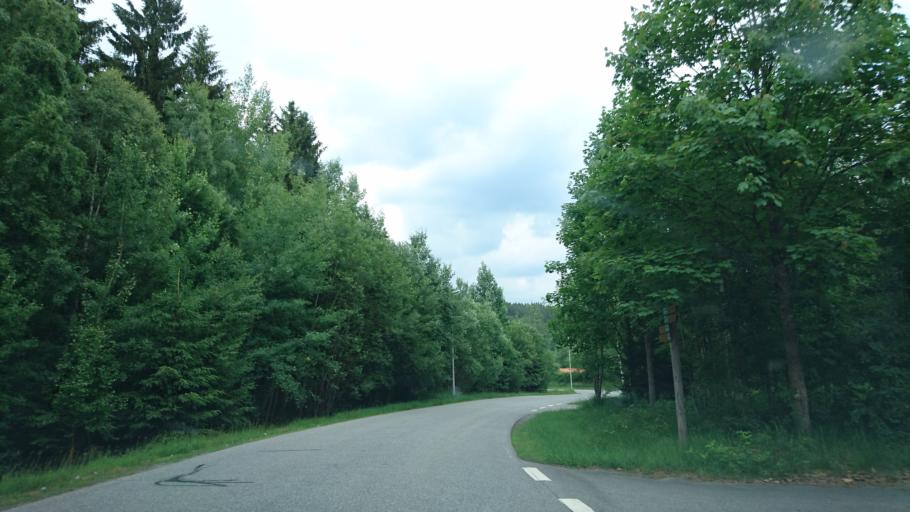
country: DE
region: Bavaria
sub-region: Lower Bavaria
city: Spiegelau
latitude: 48.9180
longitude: 13.3549
